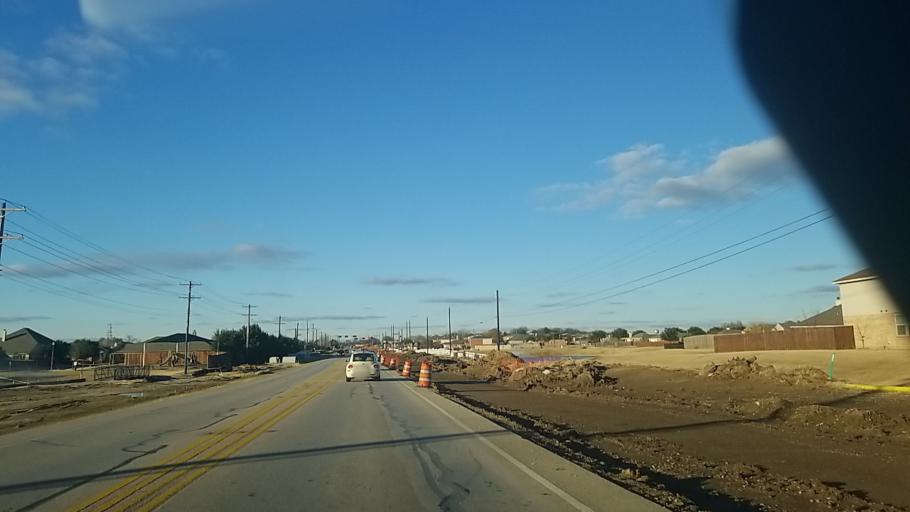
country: US
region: Texas
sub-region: Denton County
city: Corinth
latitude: 33.1513
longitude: -97.1054
